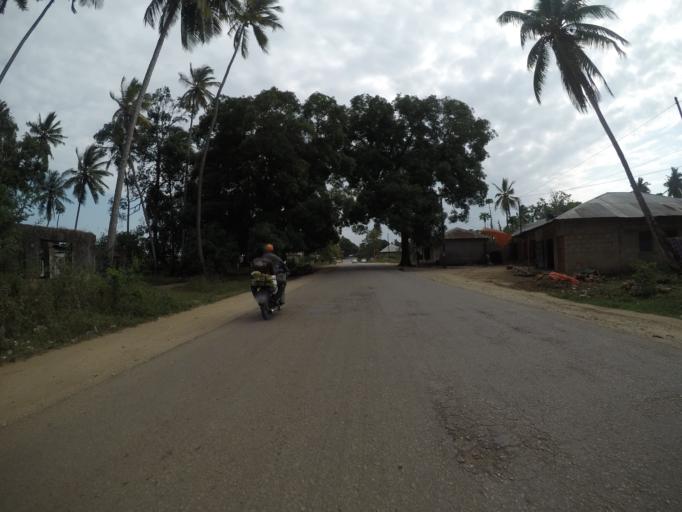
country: TZ
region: Zanzibar Central/South
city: Koani
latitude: -6.1947
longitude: 39.2992
